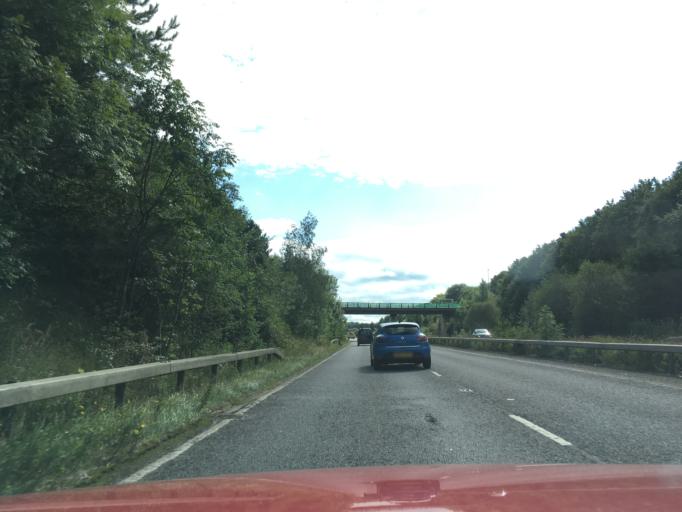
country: GB
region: England
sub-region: West Sussex
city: Horsham
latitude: 51.0695
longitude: -0.3518
